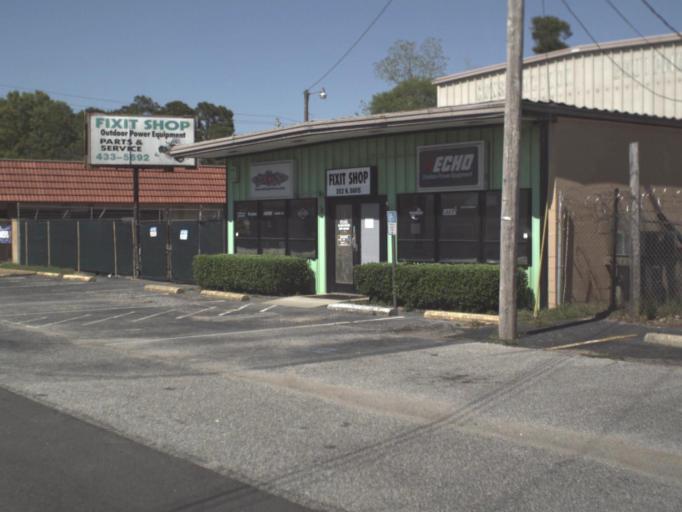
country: US
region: Florida
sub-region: Escambia County
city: Goulding
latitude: 30.4463
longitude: -87.2155
